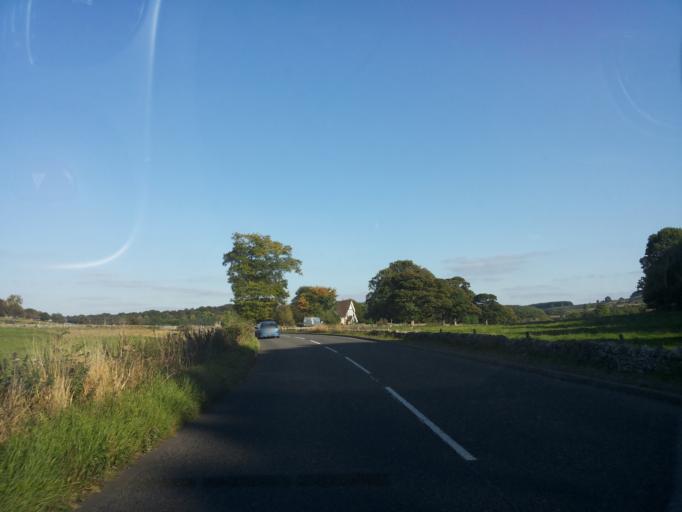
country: GB
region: England
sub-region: Derbyshire
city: Bakewell
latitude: 53.2343
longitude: -1.6838
